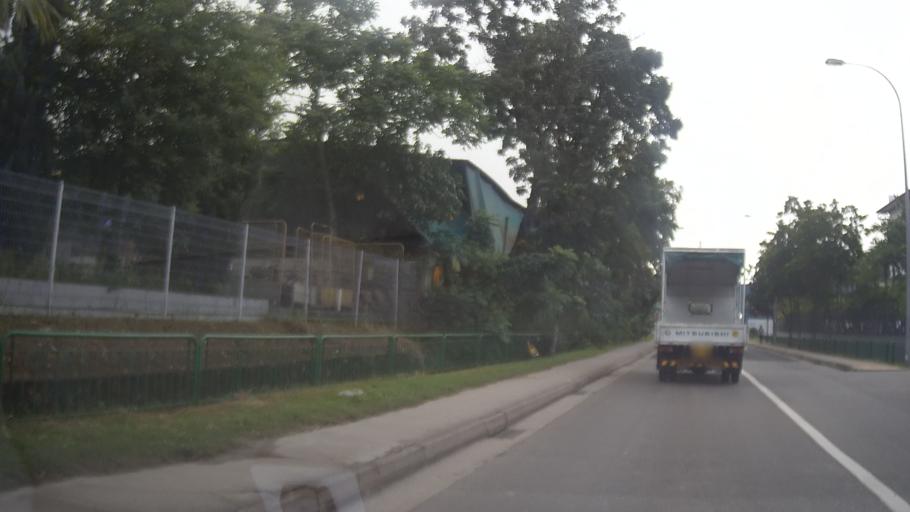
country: MY
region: Johor
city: Johor Bahru
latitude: 1.4194
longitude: 103.7497
